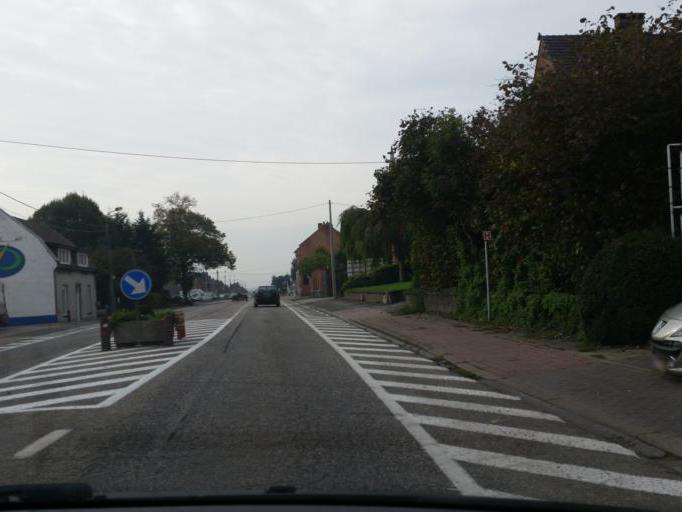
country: BE
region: Flanders
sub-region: Provincie Vlaams-Brabant
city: Halle
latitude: 50.7208
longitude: 4.2250
